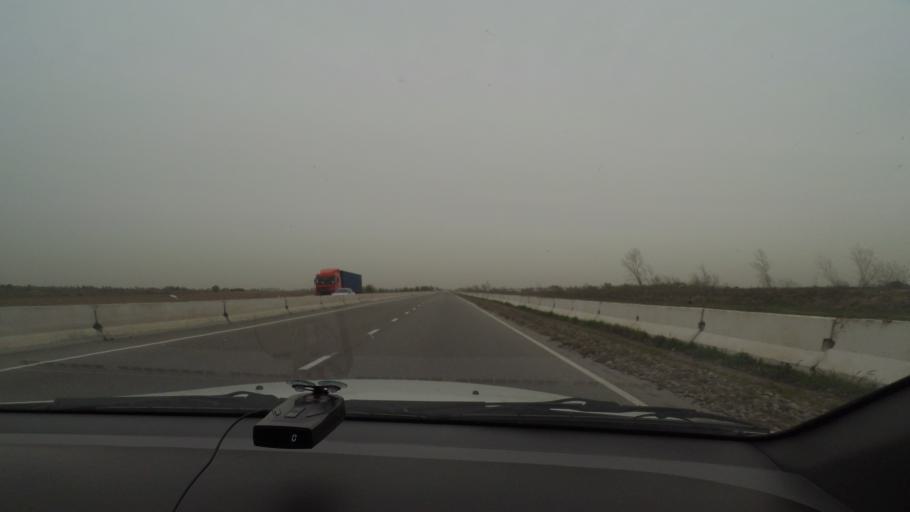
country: UZ
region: Jizzax
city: Gagarin
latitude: 40.4831
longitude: 68.2881
